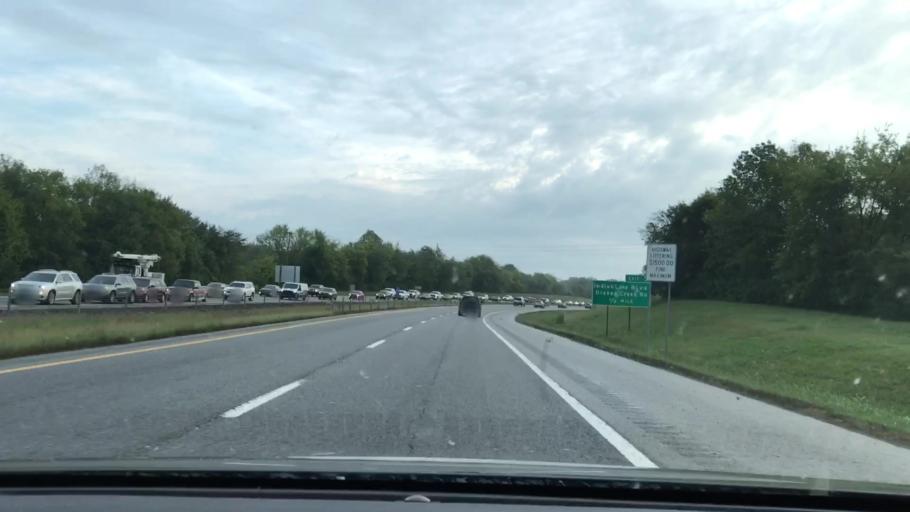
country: US
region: Tennessee
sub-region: Sumner County
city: Hendersonville
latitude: 36.3314
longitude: -86.6099
